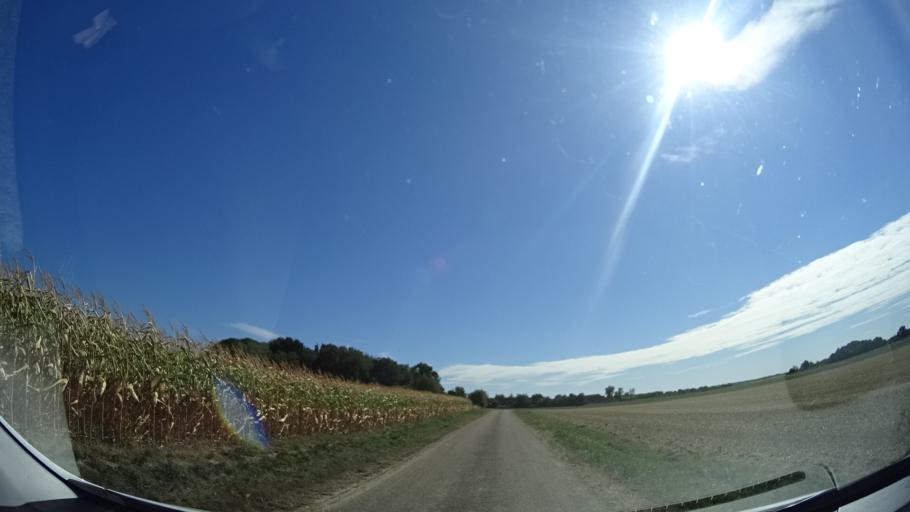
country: FR
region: Centre
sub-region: Departement du Loiret
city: Trigueres
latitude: 47.9516
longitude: 2.9632
